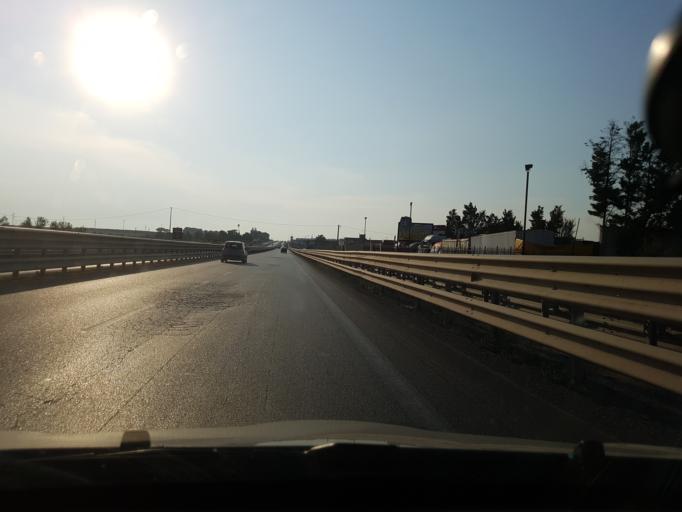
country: IT
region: Apulia
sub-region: Provincia di Foggia
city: Cerignola
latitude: 41.2764
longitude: 15.8678
